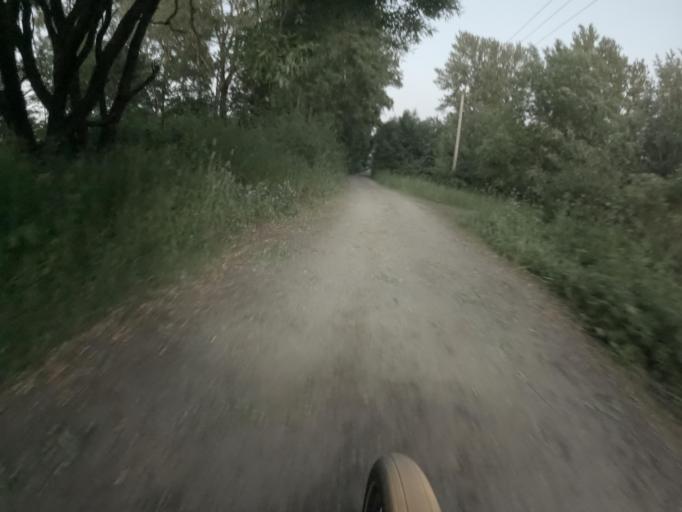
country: RU
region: Leningrad
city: Imeni Sverdlova
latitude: 59.7800
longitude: 30.6911
